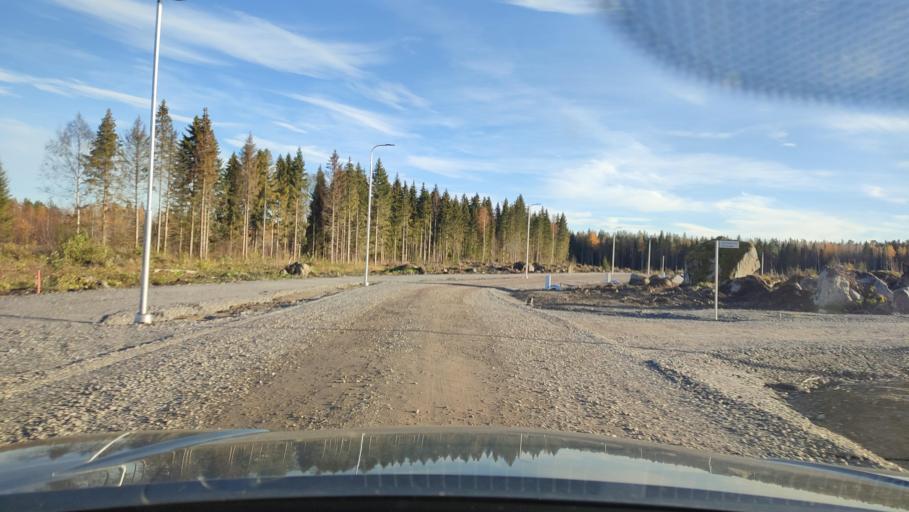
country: FI
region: Ostrobothnia
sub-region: Vaasa
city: Teeriniemi
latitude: 63.0645
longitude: 21.7015
